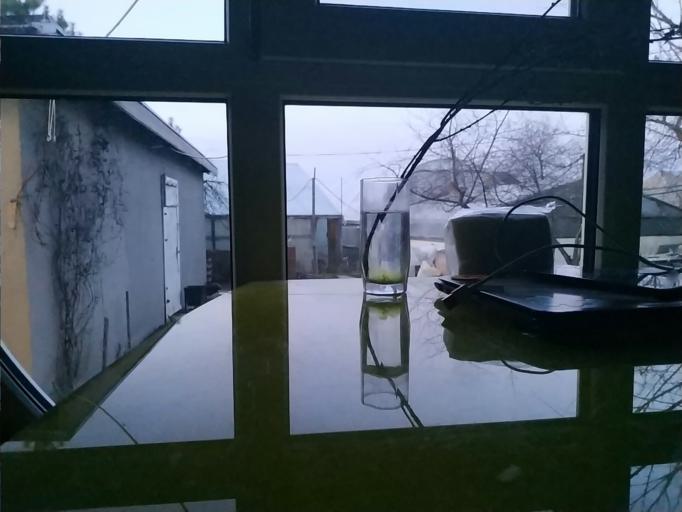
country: RU
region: Republic of Karelia
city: Sukkozero
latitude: 62.7593
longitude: 31.8627
